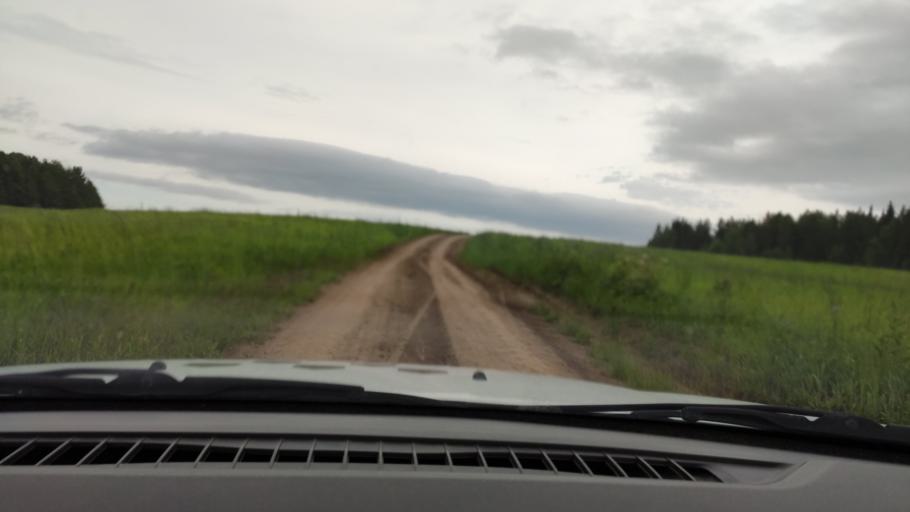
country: RU
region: Perm
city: Orda
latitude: 57.2993
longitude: 56.5915
